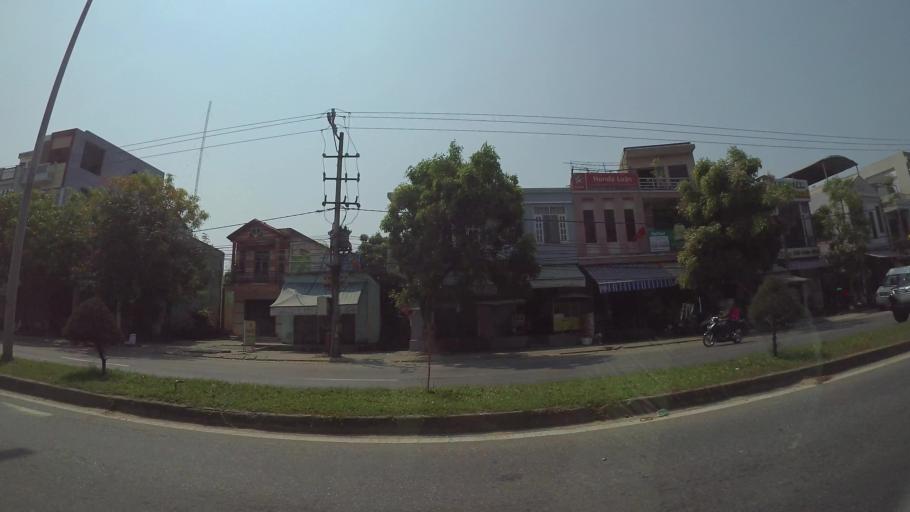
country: VN
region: Da Nang
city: Cam Le
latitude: 15.9784
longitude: 108.2083
